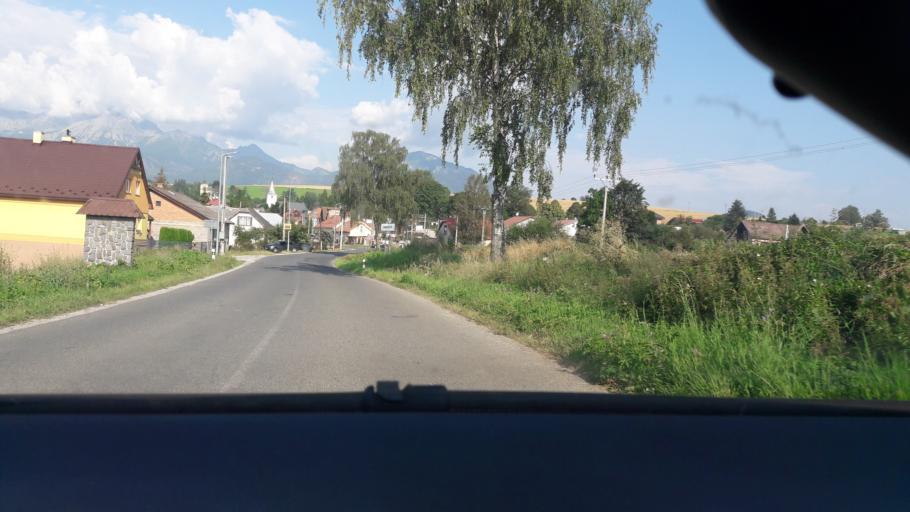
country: SK
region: Presovsky
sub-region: Okres Presov
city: Kezmarok
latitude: 49.1874
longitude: 20.3902
